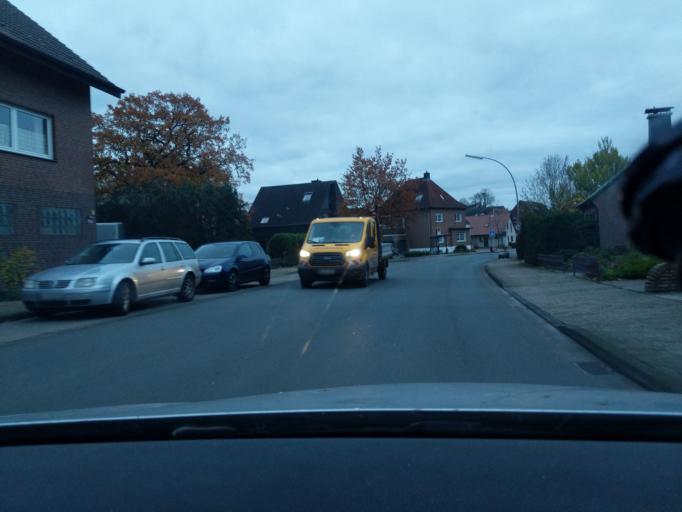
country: DE
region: North Rhine-Westphalia
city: Datteln
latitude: 51.6777
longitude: 7.4074
